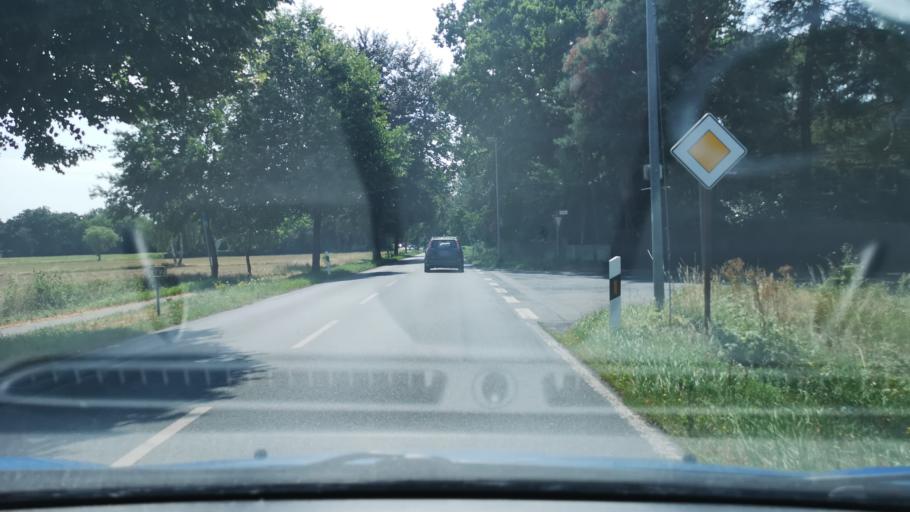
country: DE
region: Lower Saxony
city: Isernhagen Farster Bauerschaft
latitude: 52.4410
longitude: 9.8009
